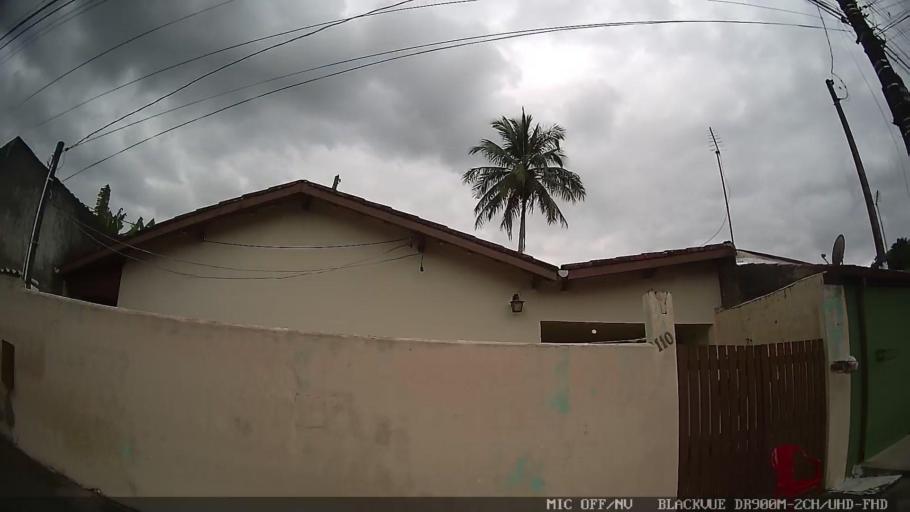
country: BR
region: Sao Paulo
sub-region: Caraguatatuba
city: Caraguatatuba
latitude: -23.6316
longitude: -45.4330
